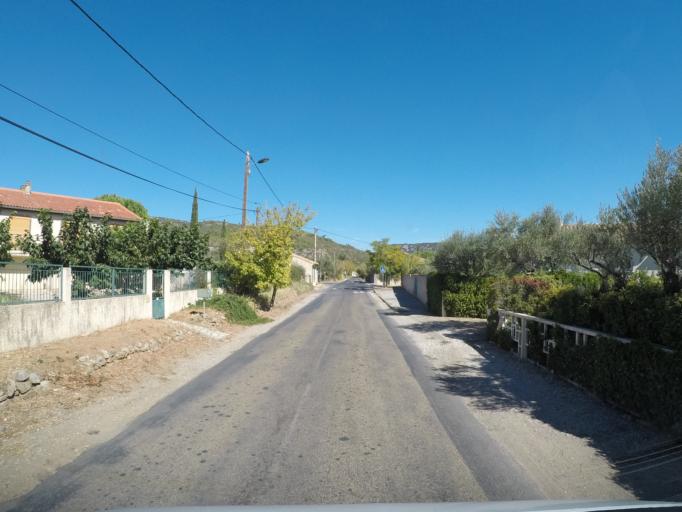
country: FR
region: Languedoc-Roussillon
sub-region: Departement de l'Herault
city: Saint-Jean-de-Fos
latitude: 43.6977
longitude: 3.5475
